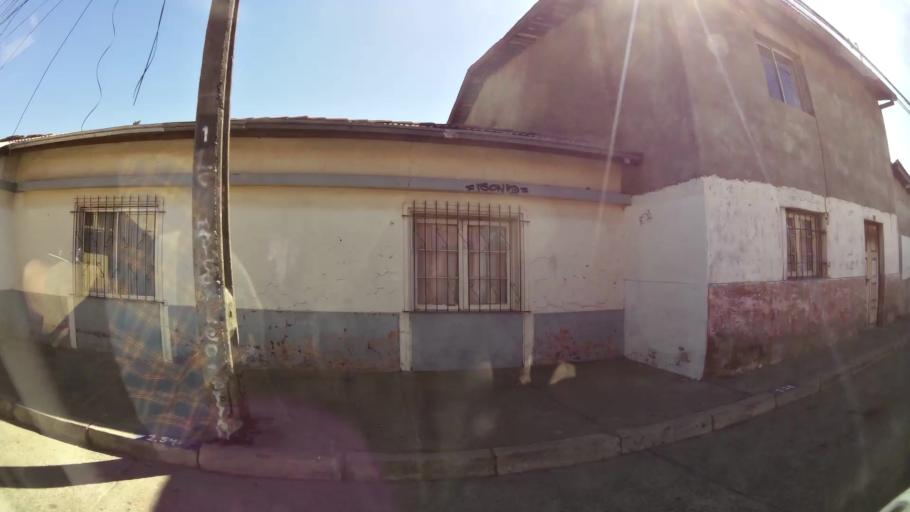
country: CL
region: O'Higgins
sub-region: Provincia de Cachapoal
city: Rancagua
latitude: -34.1768
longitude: -70.7470
